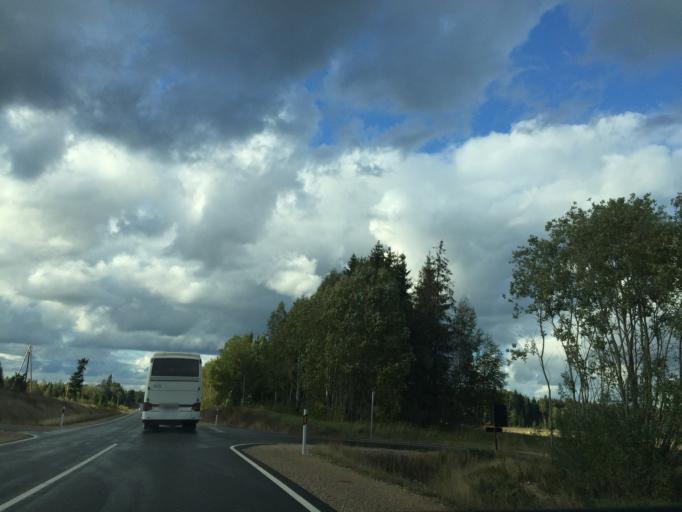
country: LV
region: Ligatne
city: Ligatne
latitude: 57.1438
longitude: 25.0788
